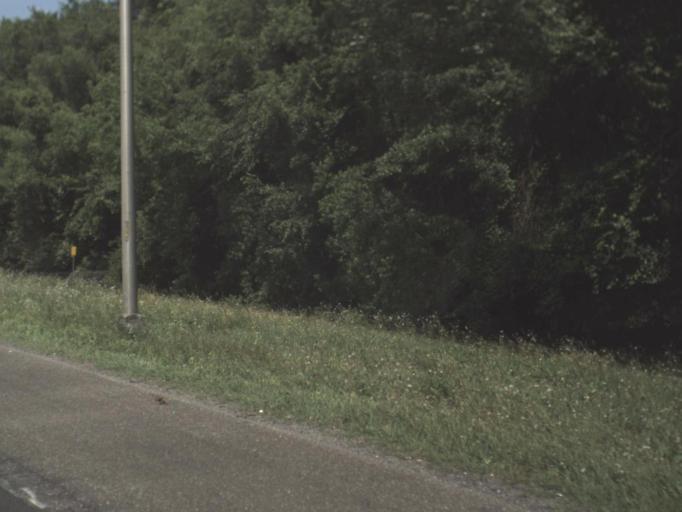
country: US
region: Florida
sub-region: Duval County
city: Jacksonville
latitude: 30.3659
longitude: -81.7608
